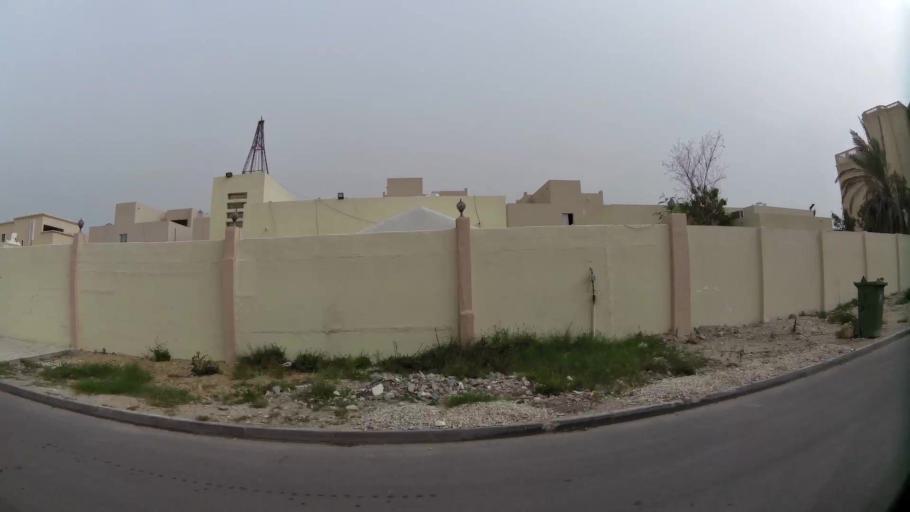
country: QA
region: Baladiyat ad Dawhah
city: Doha
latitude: 25.2462
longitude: 51.5151
